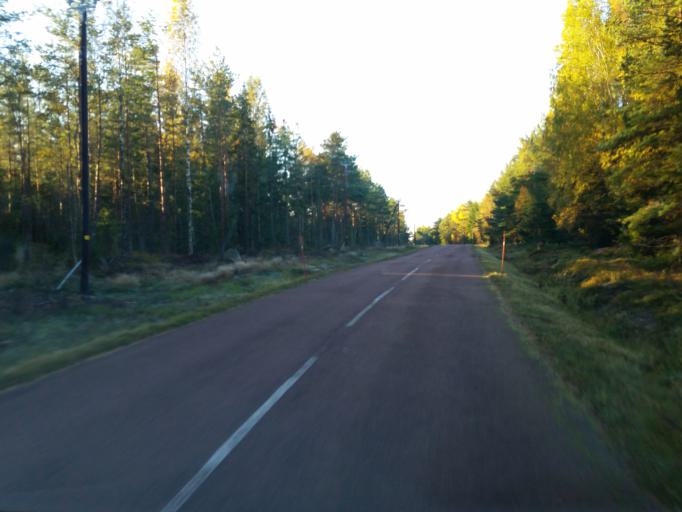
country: AX
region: Alands skaergard
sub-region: Vardoe
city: Vardoe
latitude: 60.3038
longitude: 20.3836
